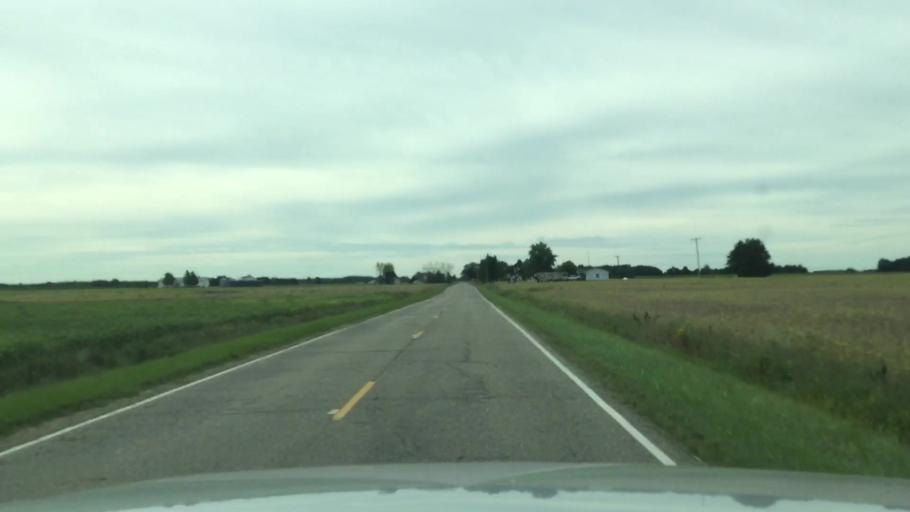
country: US
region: Michigan
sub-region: Genesee County
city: Montrose
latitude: 43.0941
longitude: -83.9878
